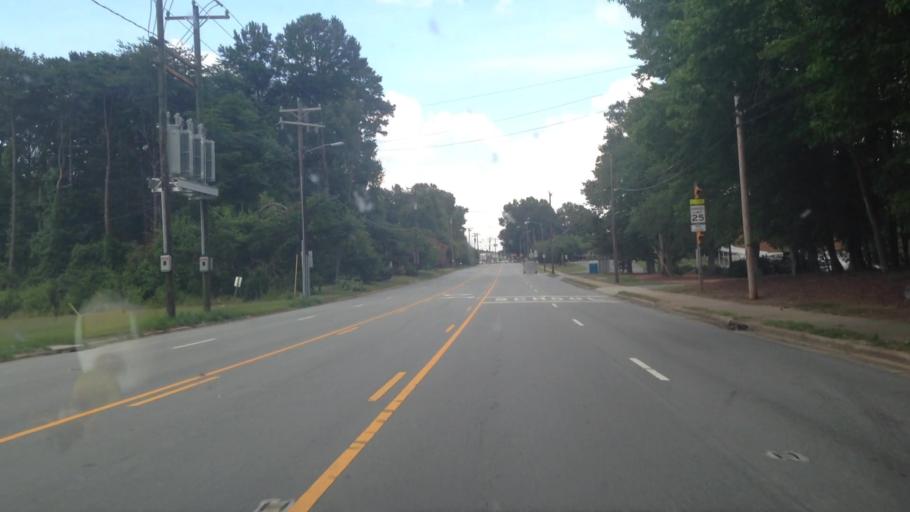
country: US
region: North Carolina
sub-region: Rockingham County
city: Mayodan
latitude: 36.4005
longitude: -79.9737
